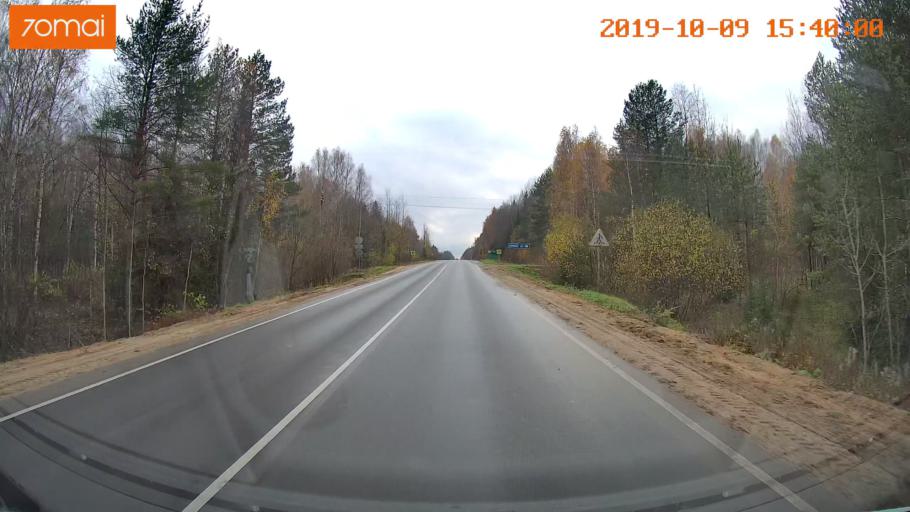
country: RU
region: Kostroma
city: Oktyabr'skiy
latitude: 57.8918
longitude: 41.1533
